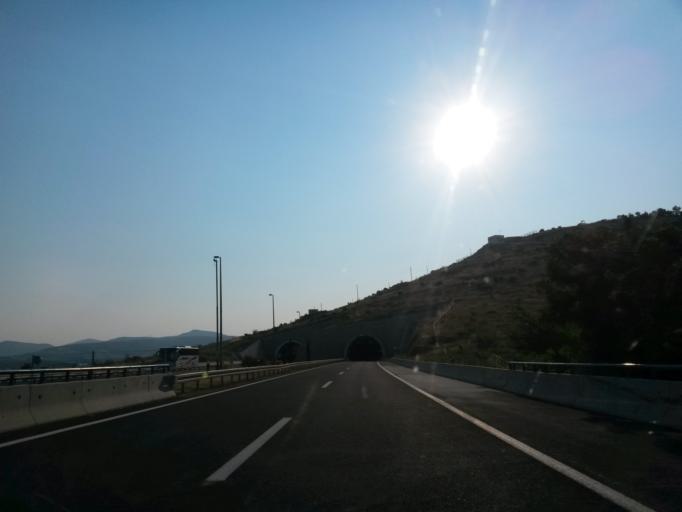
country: HR
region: Splitsko-Dalmatinska
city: Dugopolje
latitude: 43.6012
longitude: 16.5956
